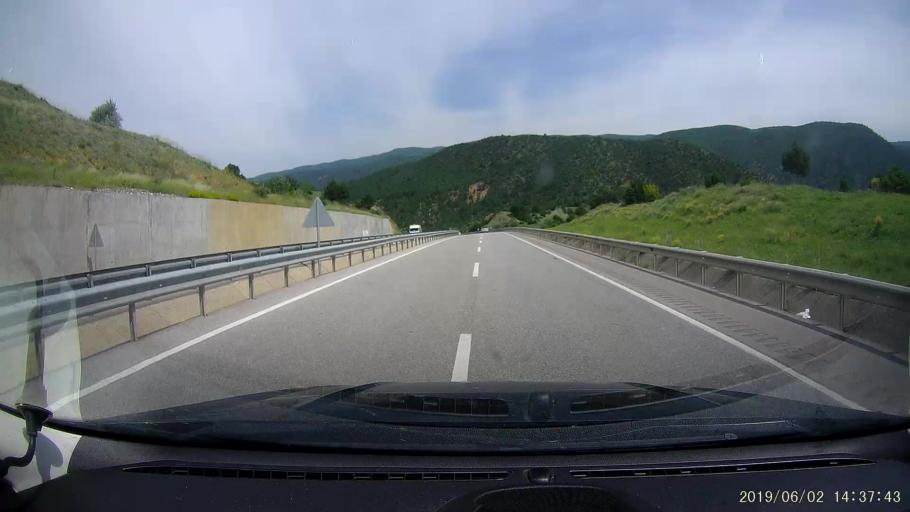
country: TR
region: Corum
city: Hacihamza
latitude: 41.0514
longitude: 34.2638
